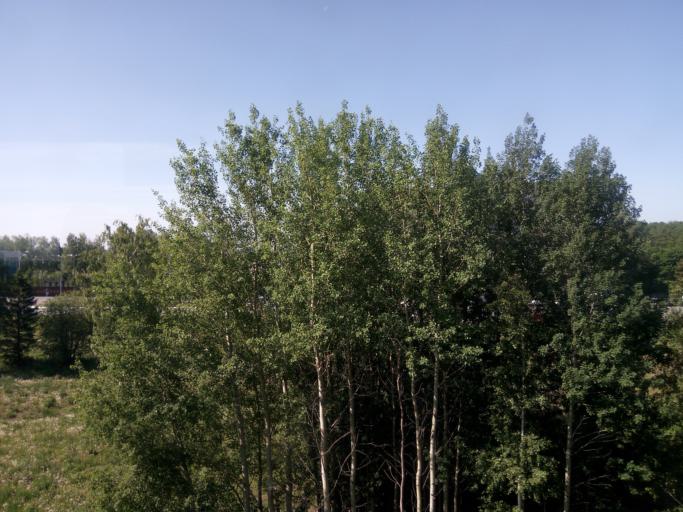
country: RU
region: Tatarstan
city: Stolbishchi
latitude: 55.6115
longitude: 49.2937
